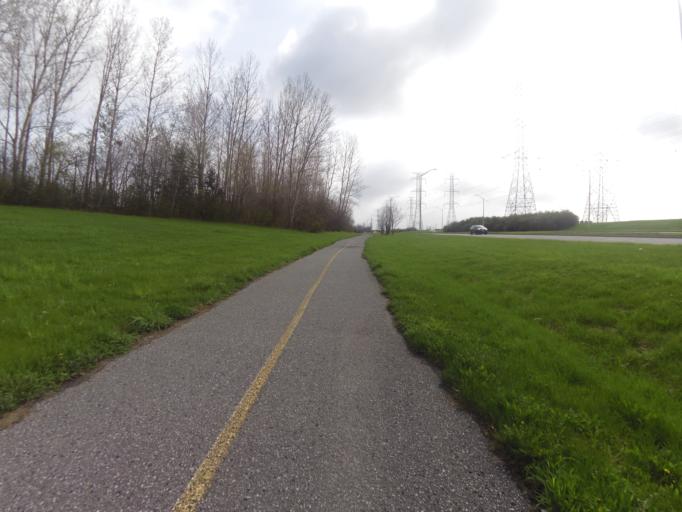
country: CA
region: Ontario
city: Bells Corners
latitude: 45.3238
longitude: -75.7658
